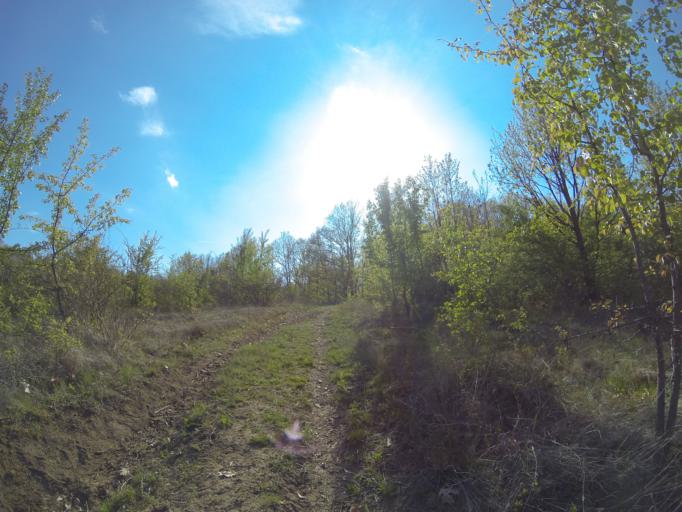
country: RO
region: Gorj
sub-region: Comuna Crusetu
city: Crusetu
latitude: 44.6230
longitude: 23.6316
